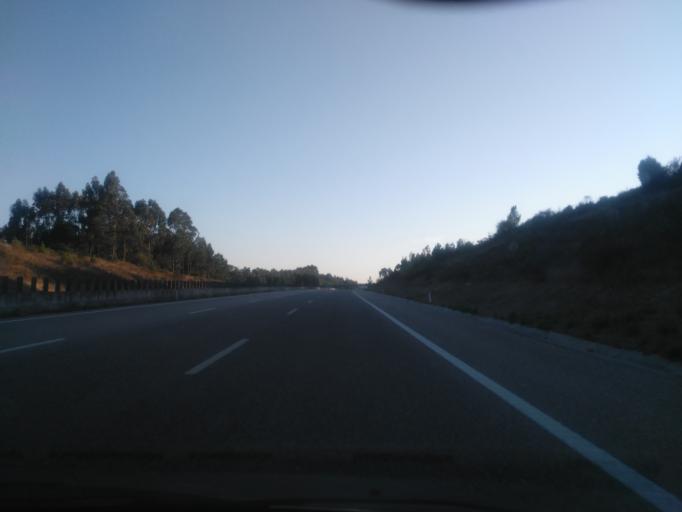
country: PT
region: Coimbra
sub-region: Figueira da Foz
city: Lavos
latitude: 40.0798
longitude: -8.7717
